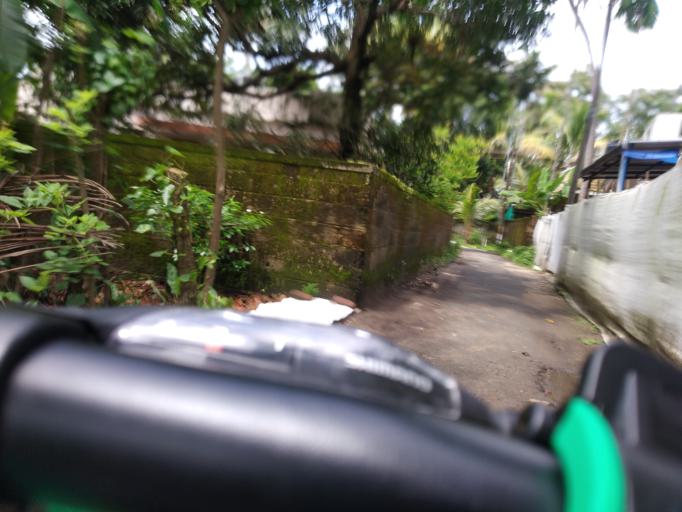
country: IN
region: Kerala
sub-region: Ernakulam
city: Elur
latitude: 10.0793
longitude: 76.2153
